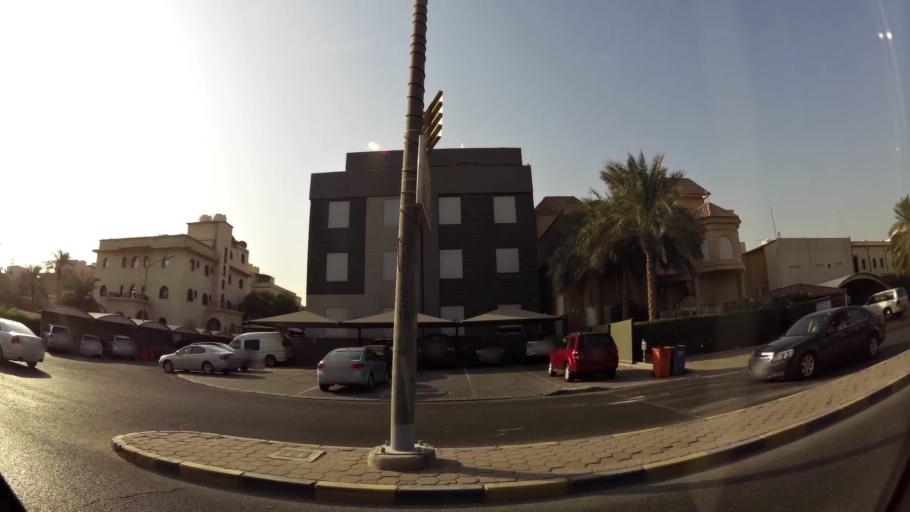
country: KW
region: Al Asimah
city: Ad Dasmah
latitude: 29.3628
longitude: 48.0047
